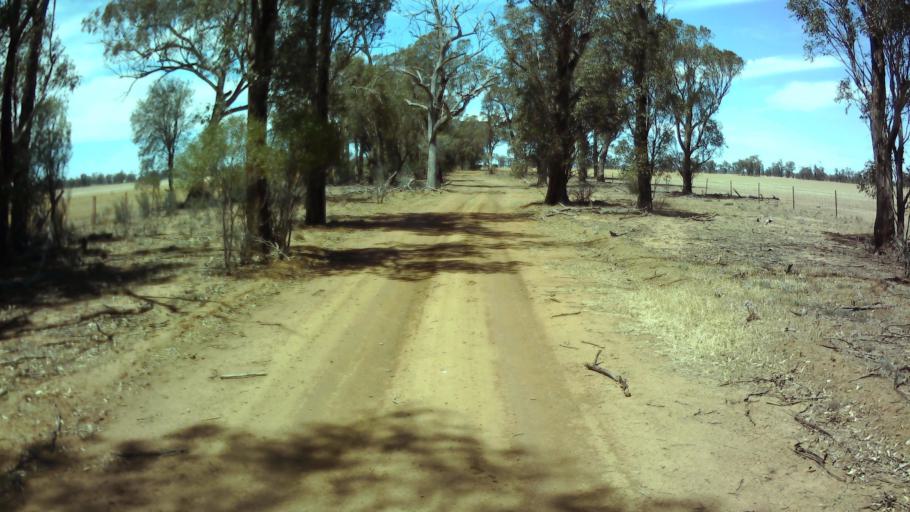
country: AU
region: New South Wales
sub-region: Weddin
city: Grenfell
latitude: -33.9230
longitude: 147.8043
